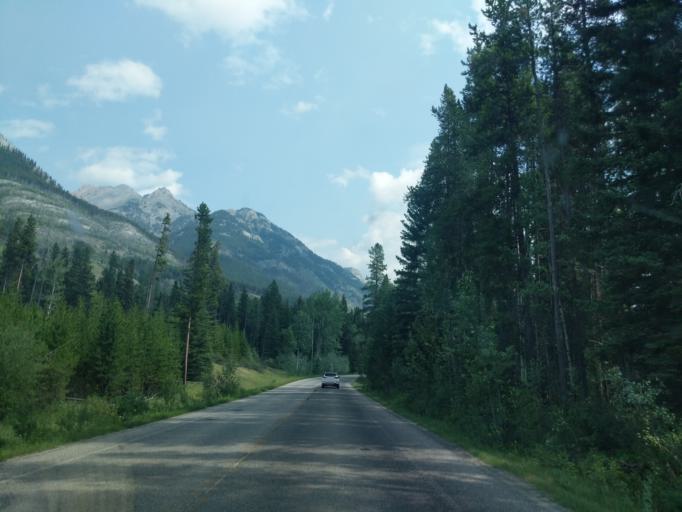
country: CA
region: Alberta
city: Banff
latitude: 51.2081
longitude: -115.7548
